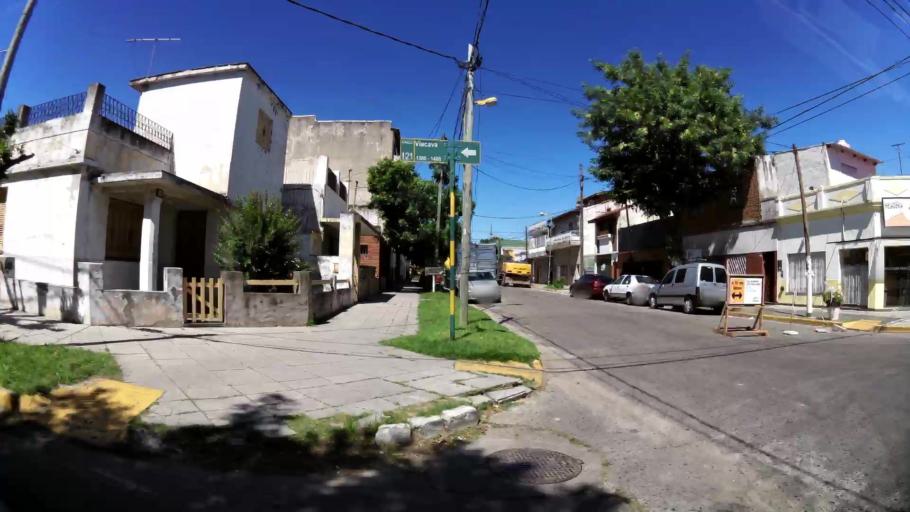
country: AR
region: Buenos Aires
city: Caseros
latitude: -34.5908
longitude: -58.5444
